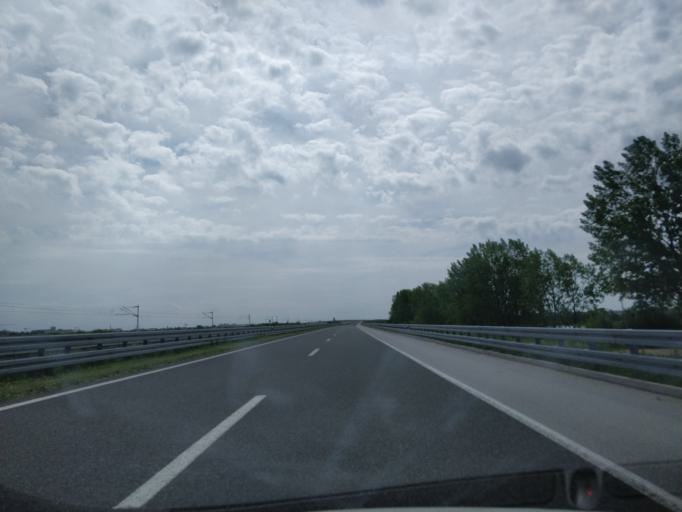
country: HR
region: Grad Zagreb
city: Odra
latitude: 45.7228
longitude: 16.0265
